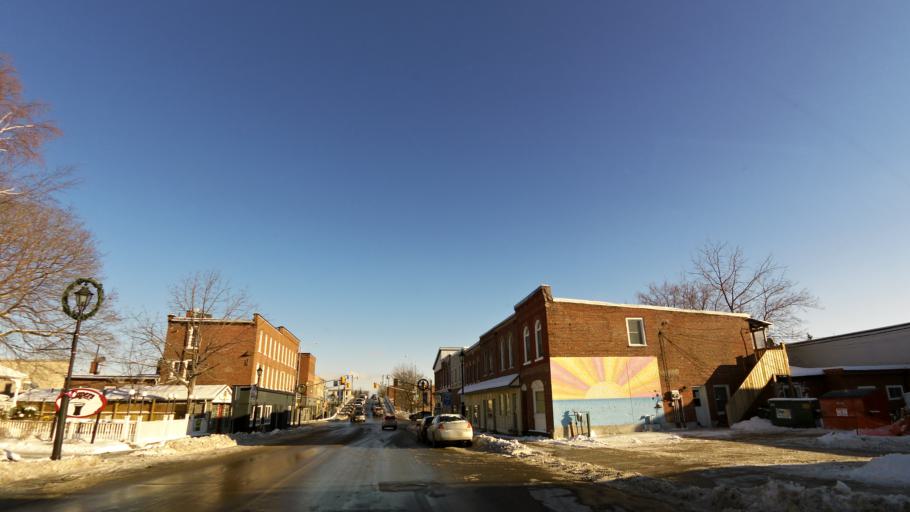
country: CA
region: Ontario
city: Quinte West
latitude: 44.3085
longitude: -77.8013
